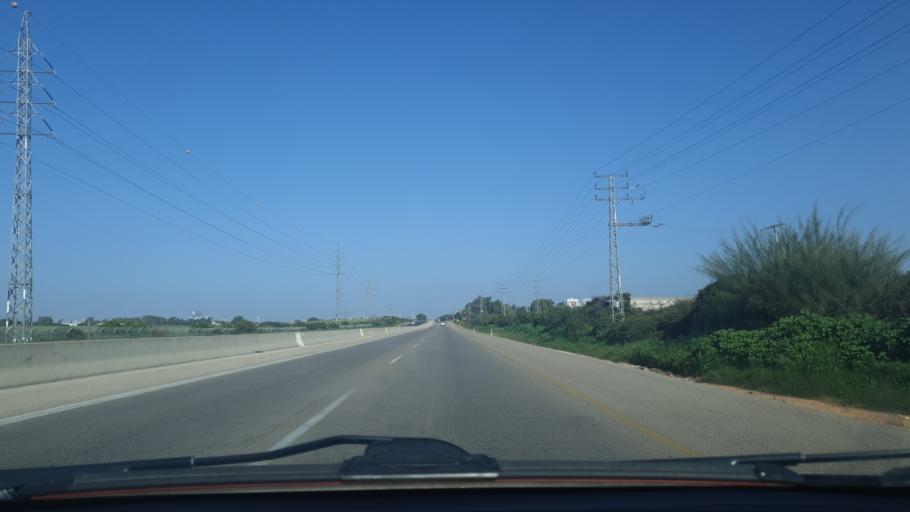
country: IL
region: Central District
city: Kefar Habad
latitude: 31.9814
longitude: 34.8351
